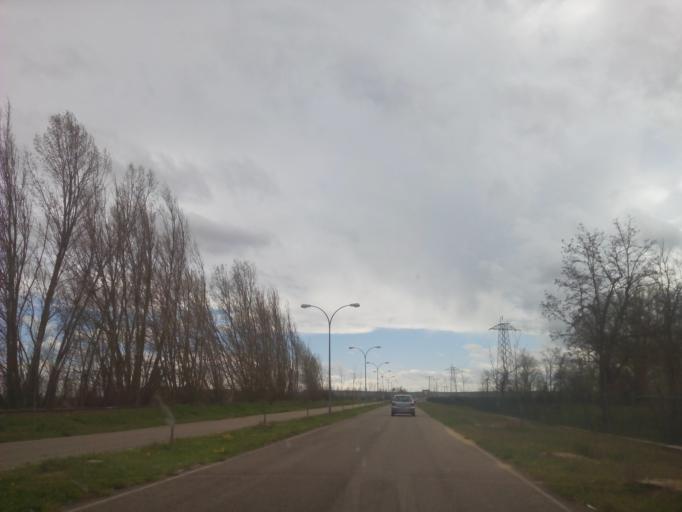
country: ES
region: Castille and Leon
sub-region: Provincia de Salamanca
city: Encinas de Abajo
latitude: 40.9399
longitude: -5.4945
